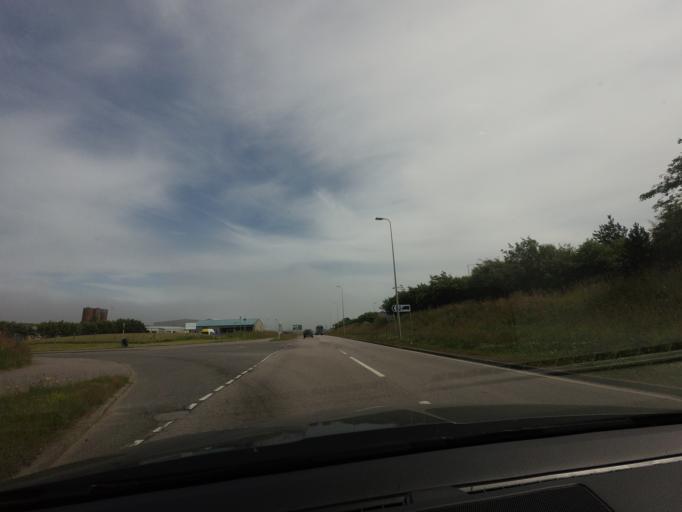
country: GB
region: Scotland
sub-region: Aberdeenshire
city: Peterhead
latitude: 57.4871
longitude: -1.8078
